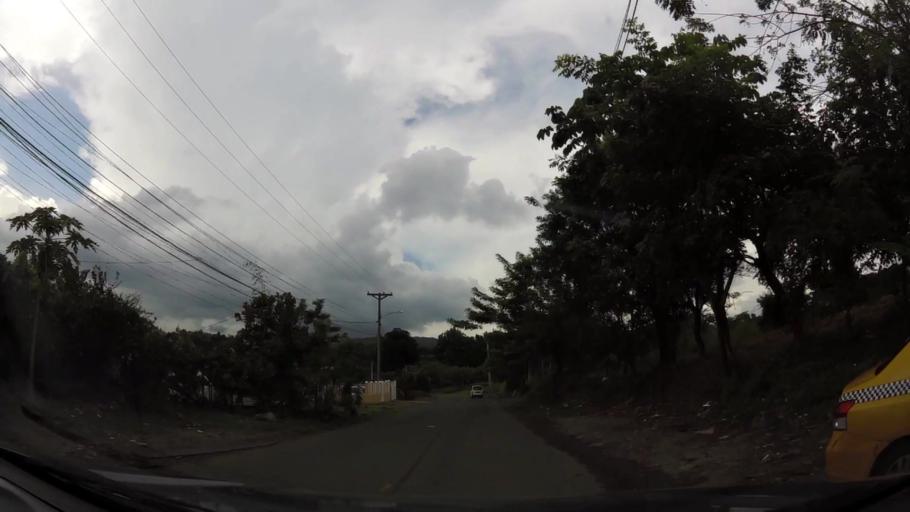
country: PA
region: Panama
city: Cabra Numero Uno
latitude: 9.1198
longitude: -79.3570
